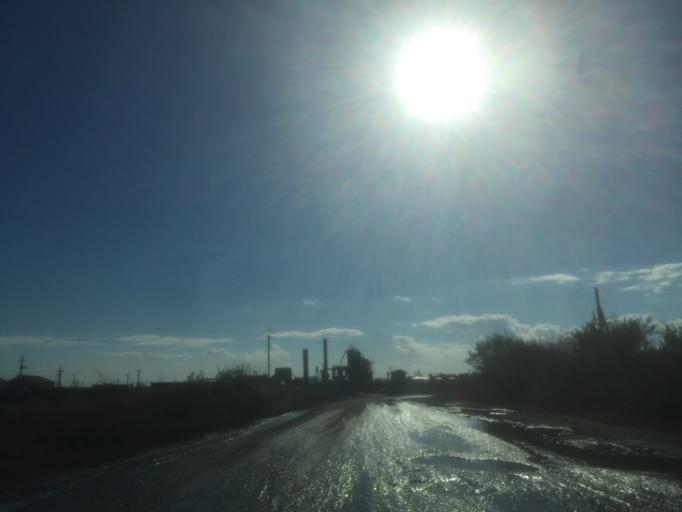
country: KZ
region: Astana Qalasy
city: Astana
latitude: 51.2148
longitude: 71.3544
